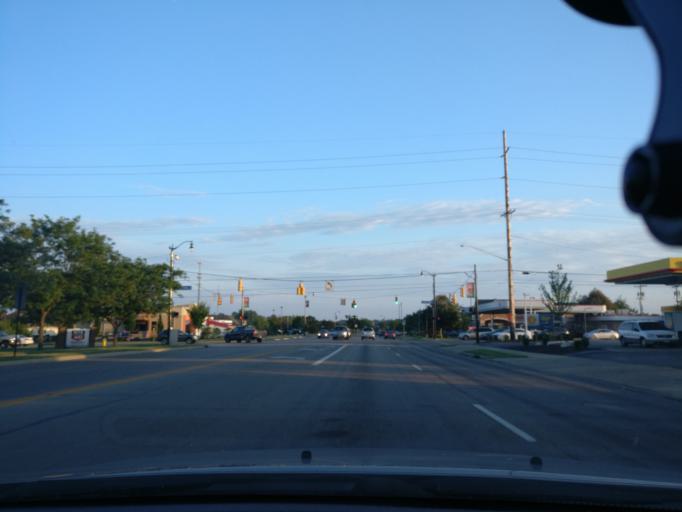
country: US
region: Ohio
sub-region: Montgomery County
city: Centerville
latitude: 39.6142
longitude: -84.1603
